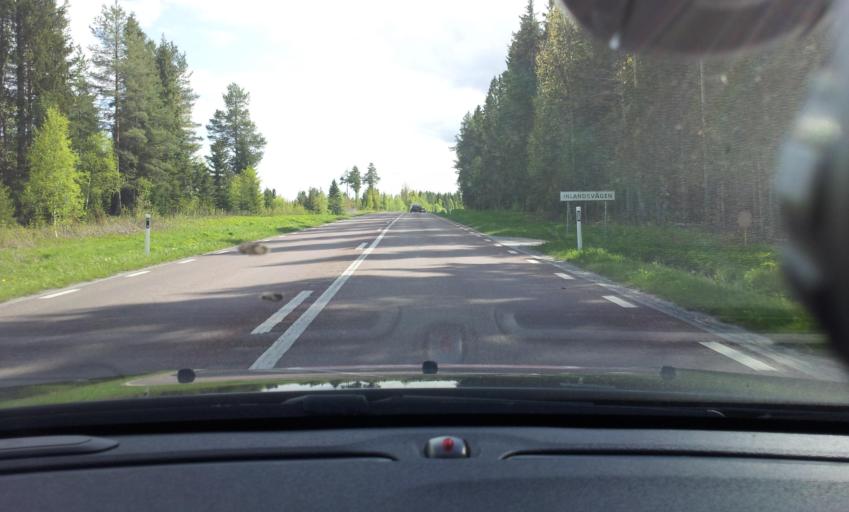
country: SE
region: Jaemtland
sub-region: OEstersunds Kommun
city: Brunflo
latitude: 63.0613
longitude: 14.8348
